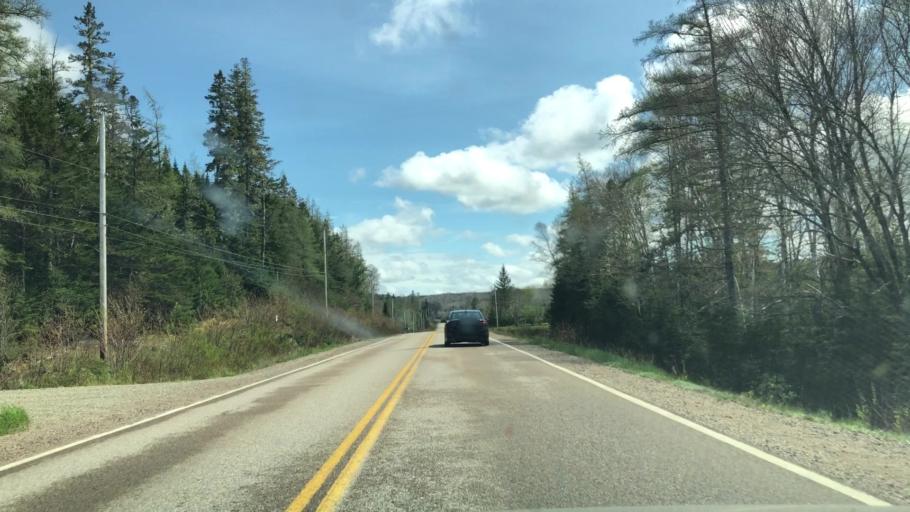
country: CA
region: Nova Scotia
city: Antigonish
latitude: 45.2082
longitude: -62.0038
